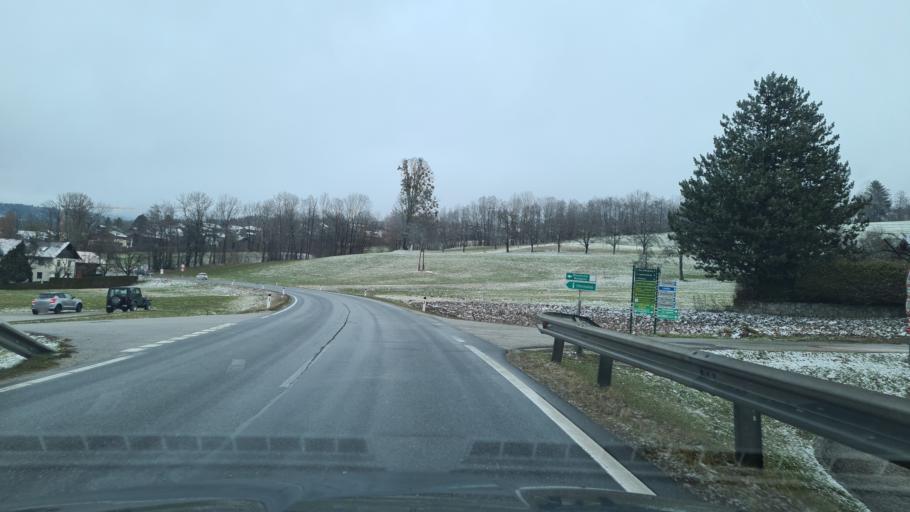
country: AT
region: Upper Austria
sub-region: Politischer Bezirk Vocklabruck
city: Zell am Moos
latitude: 47.9005
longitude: 13.3199
